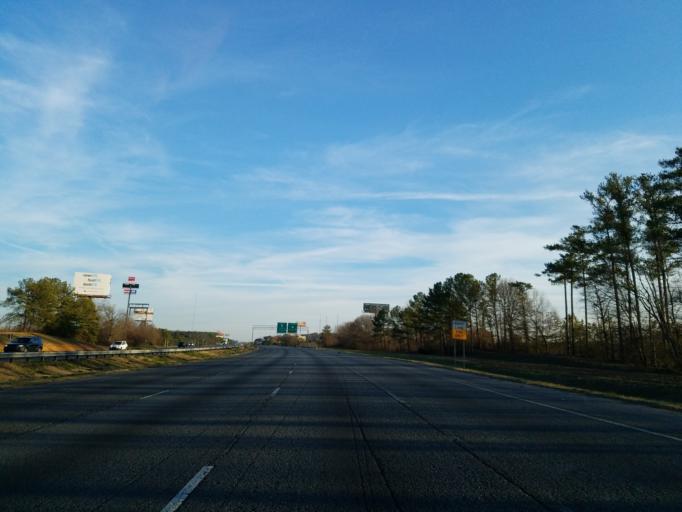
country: US
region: Georgia
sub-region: Gordon County
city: Calhoun
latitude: 34.5607
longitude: -84.9397
